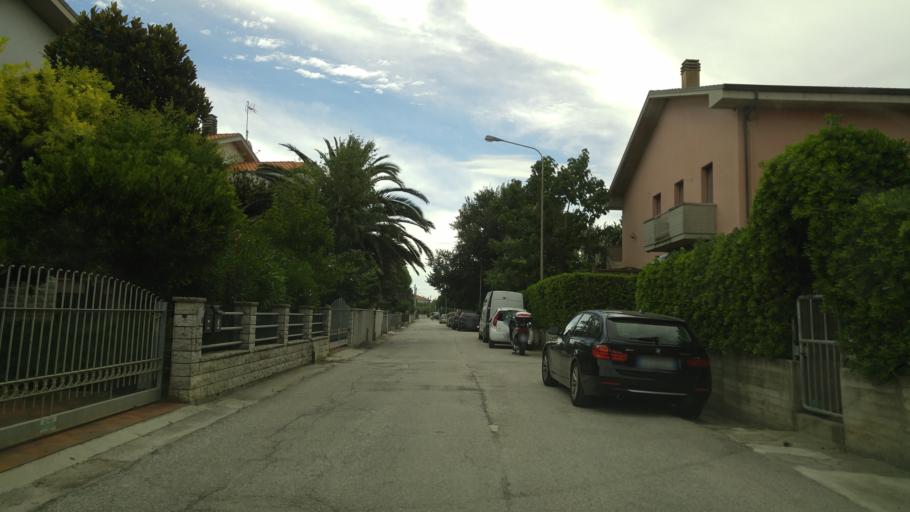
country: IT
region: The Marches
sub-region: Provincia di Pesaro e Urbino
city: Centinarola
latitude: 43.8601
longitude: 12.9910
